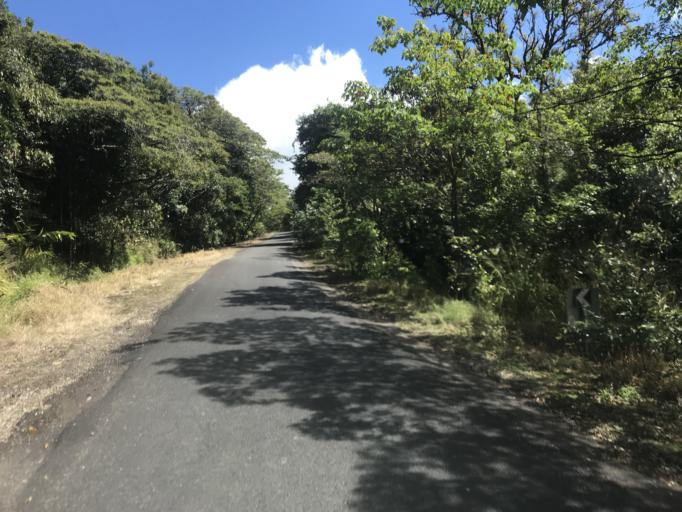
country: AU
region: Queensland
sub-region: Tablelands
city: Ravenshoe
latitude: -17.5203
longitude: 145.5666
